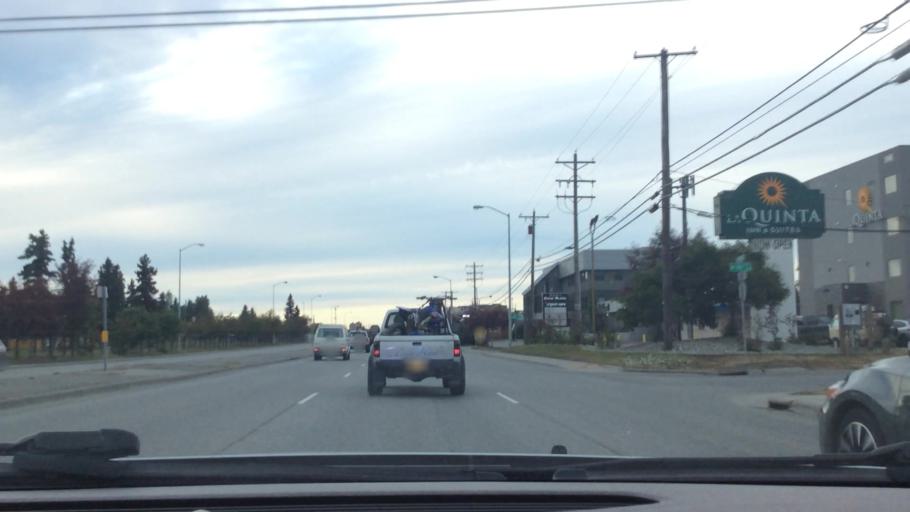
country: US
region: Alaska
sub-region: Anchorage Municipality
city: Anchorage
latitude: 61.1879
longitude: -149.9129
